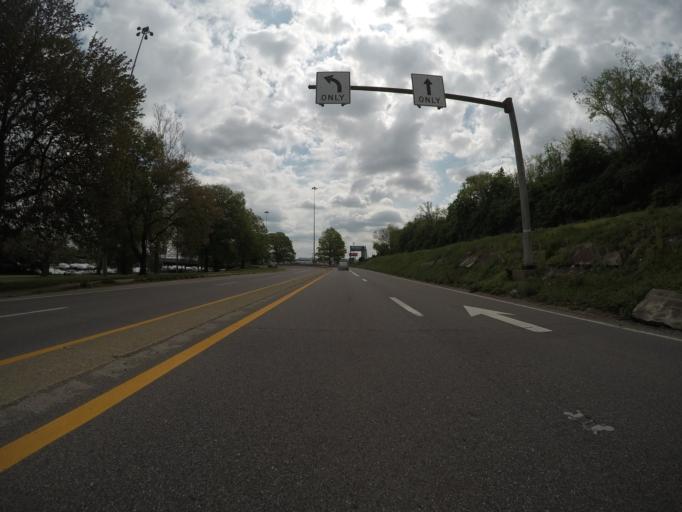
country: US
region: West Virginia
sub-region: Kanawha County
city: South Charleston
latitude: 38.3636
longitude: -81.6720
